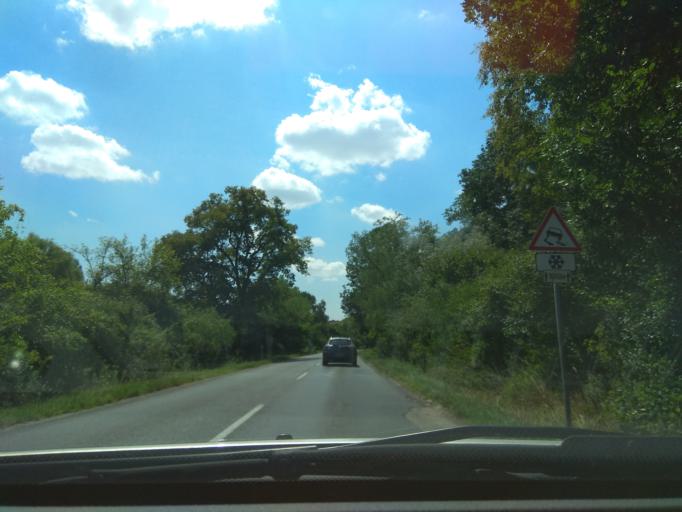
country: HU
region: Borsod-Abauj-Zemplen
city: Harsany
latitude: 48.0033
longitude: 20.7605
